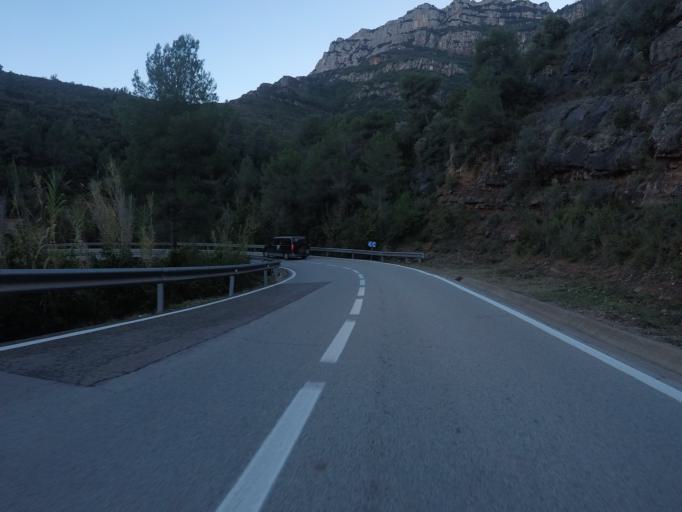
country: ES
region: Catalonia
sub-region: Provincia de Barcelona
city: Monistrol de Montserrat
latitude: 41.6083
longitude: 1.8373
